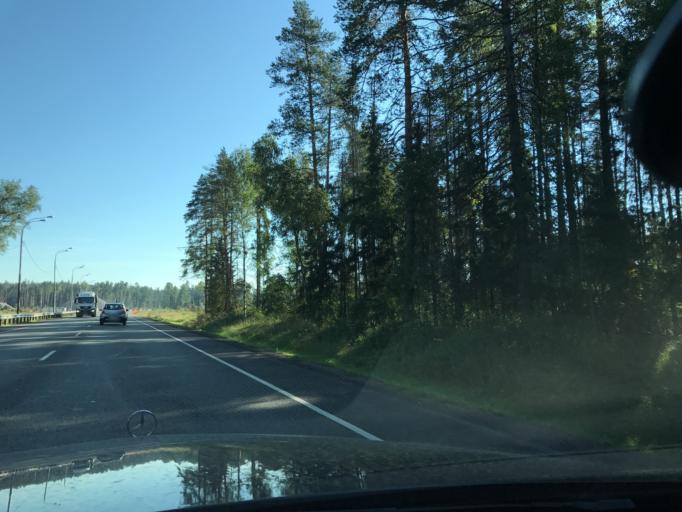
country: RU
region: Moskovskaya
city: Chernogolovka
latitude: 55.9756
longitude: 38.3032
